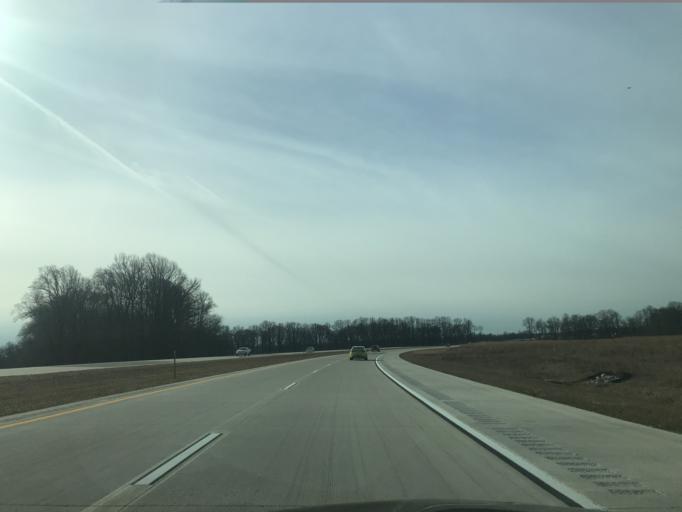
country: US
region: Delaware
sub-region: New Castle County
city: Middletown
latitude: 39.5005
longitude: -75.6958
